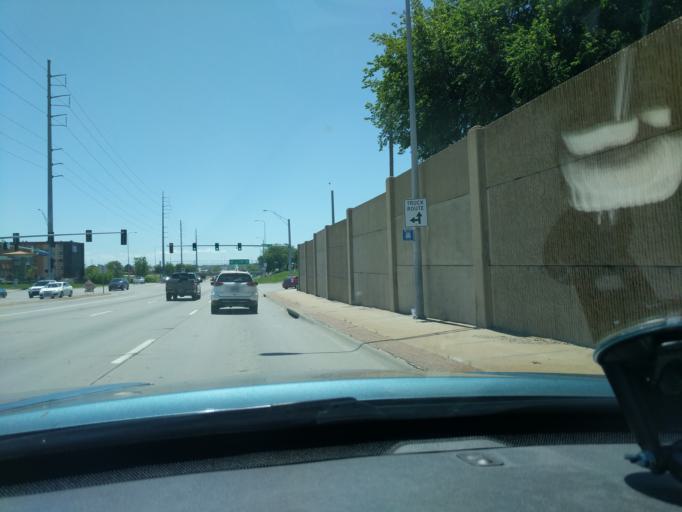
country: US
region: Nebraska
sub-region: Douglas County
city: Ralston
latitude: 41.2278
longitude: -96.0240
